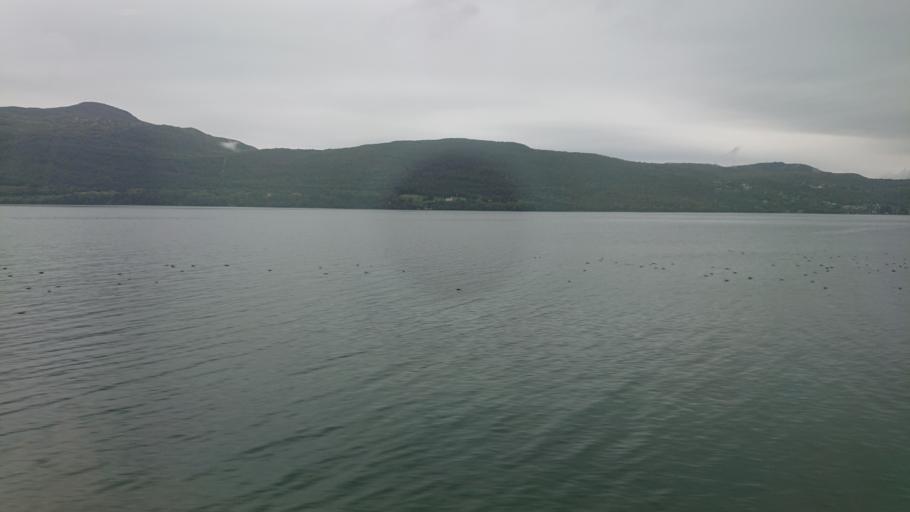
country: FR
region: Rhone-Alpes
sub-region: Departement de la Savoie
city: Chatillon
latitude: 45.7806
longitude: 5.8641
